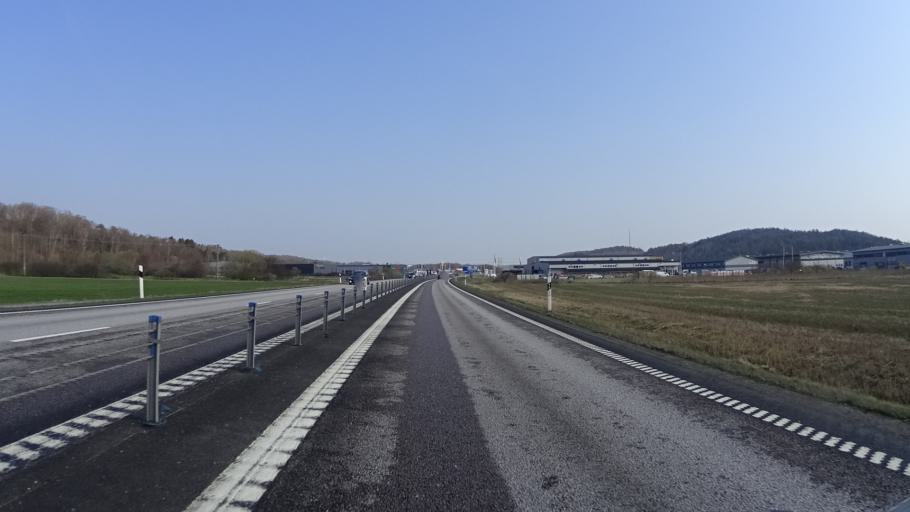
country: SE
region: Halland
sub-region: Varbergs Kommun
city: Varberg
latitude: 57.1617
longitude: 12.2730
